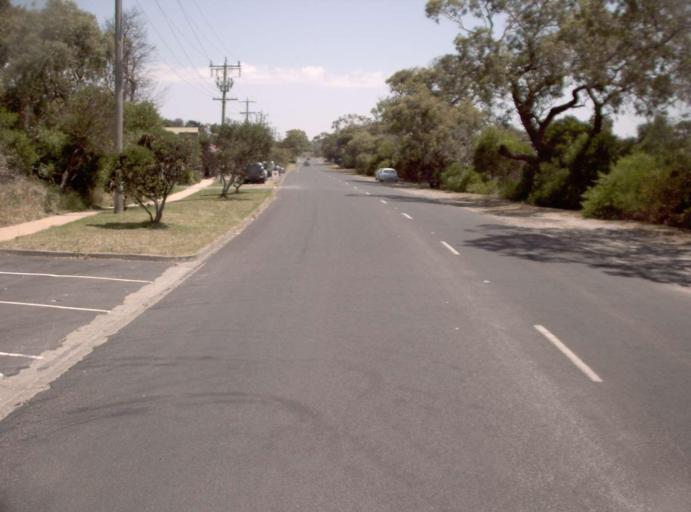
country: AU
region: Victoria
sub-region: Bass Coast
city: North Wonthaggi
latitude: -38.7001
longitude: 145.8683
